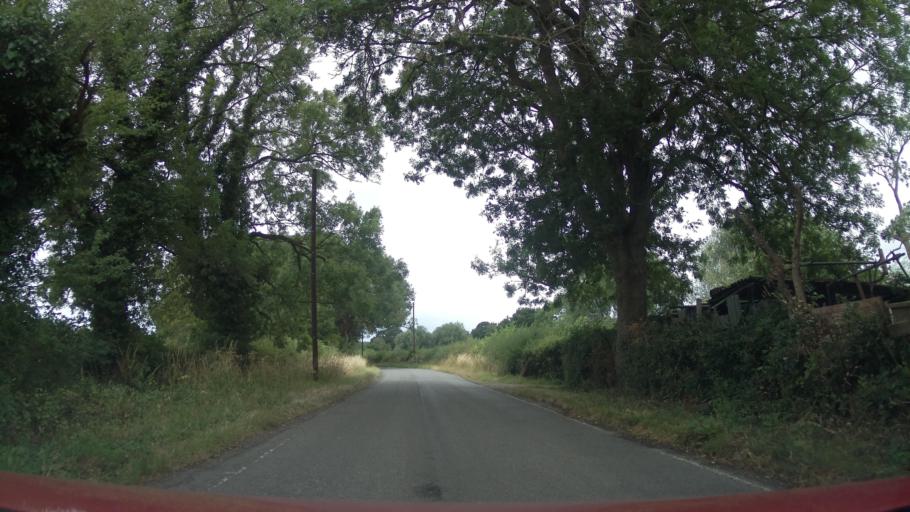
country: GB
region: England
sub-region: Derbyshire
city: Findern
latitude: 52.8798
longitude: -1.5345
